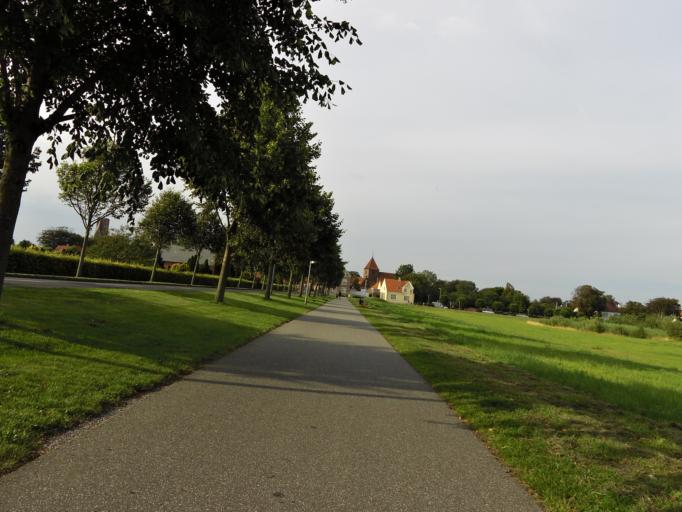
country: DK
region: South Denmark
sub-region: Esbjerg Kommune
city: Ribe
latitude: 55.3239
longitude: 8.7639
